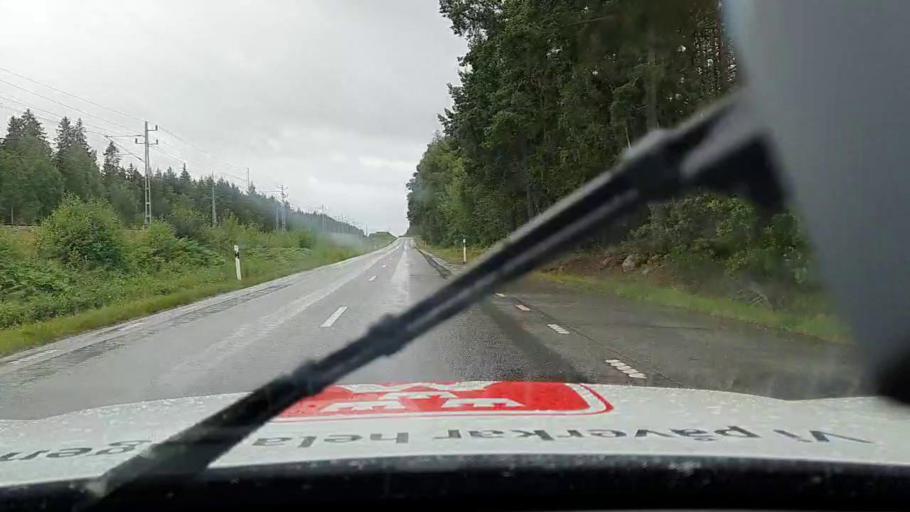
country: SE
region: Vaestra Goetaland
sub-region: Toreboda Kommun
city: Toereboda
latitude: 58.6719
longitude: 14.0973
